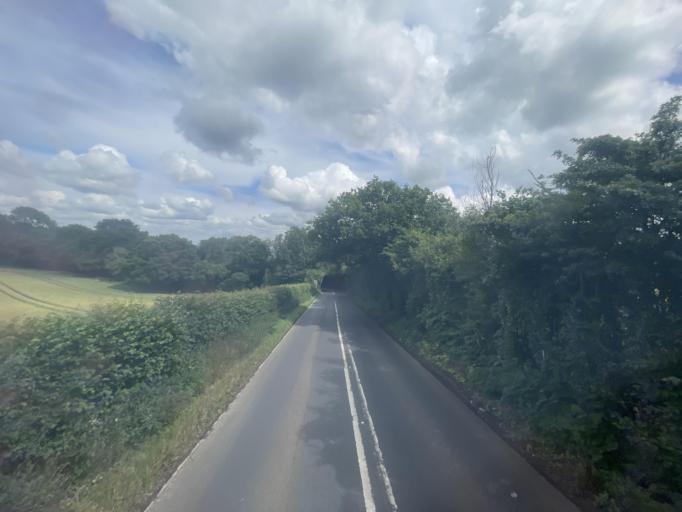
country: GB
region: England
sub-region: Kent
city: Westerham
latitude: 51.2879
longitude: 0.0609
